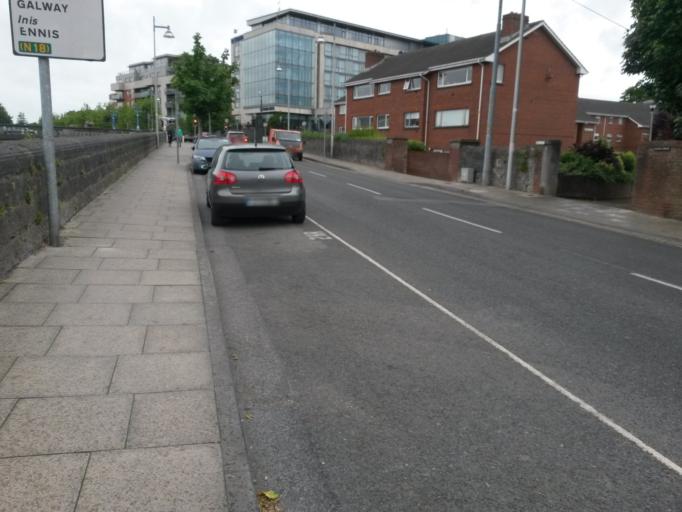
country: IE
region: Munster
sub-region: County Limerick
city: Luimneach
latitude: 52.6663
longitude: -8.6300
